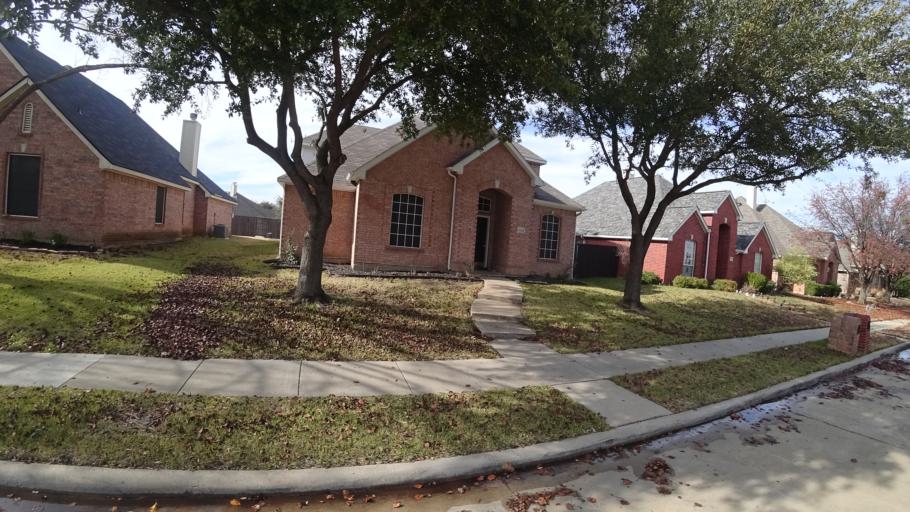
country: US
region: Texas
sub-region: Denton County
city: Highland Village
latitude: 33.0681
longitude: -97.0442
